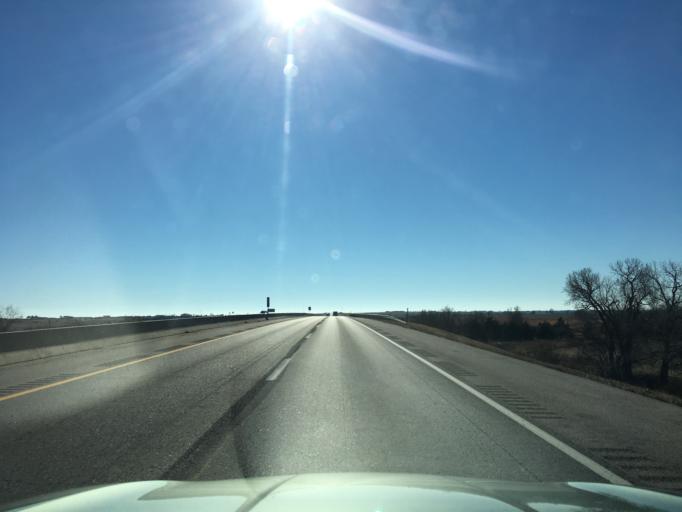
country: US
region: Kansas
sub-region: Sumner County
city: Wellington
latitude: 37.0748
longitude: -97.3386
